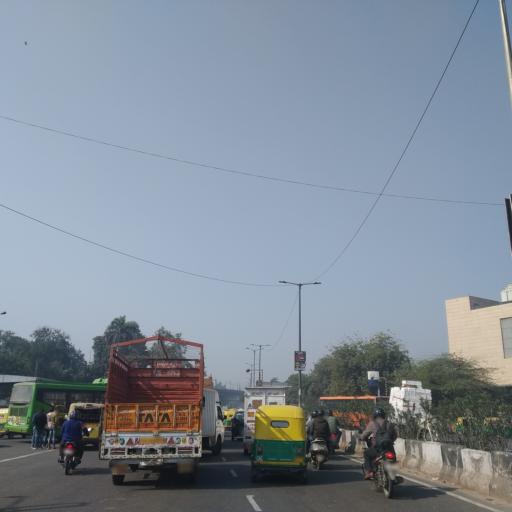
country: IN
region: NCT
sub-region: North Delhi
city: Delhi
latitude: 28.6689
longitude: 77.2274
